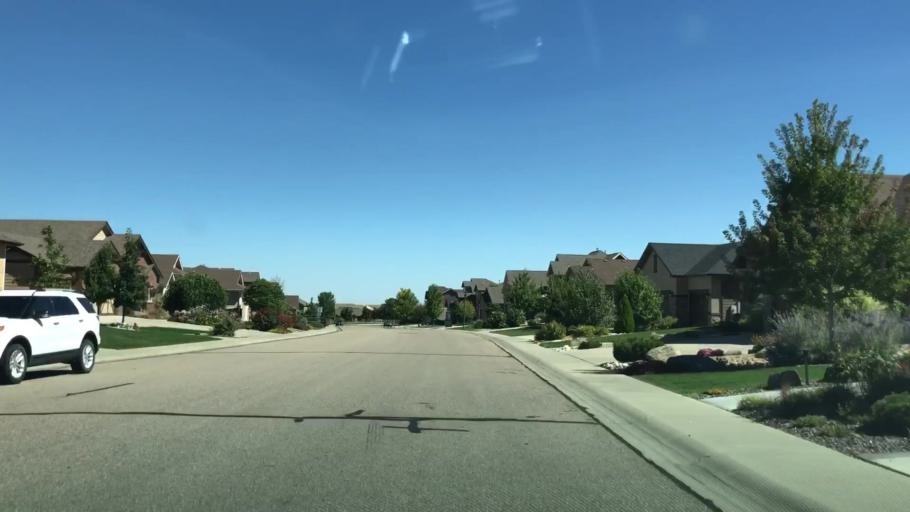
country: US
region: Colorado
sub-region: Weld County
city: Windsor
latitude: 40.4510
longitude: -104.9544
